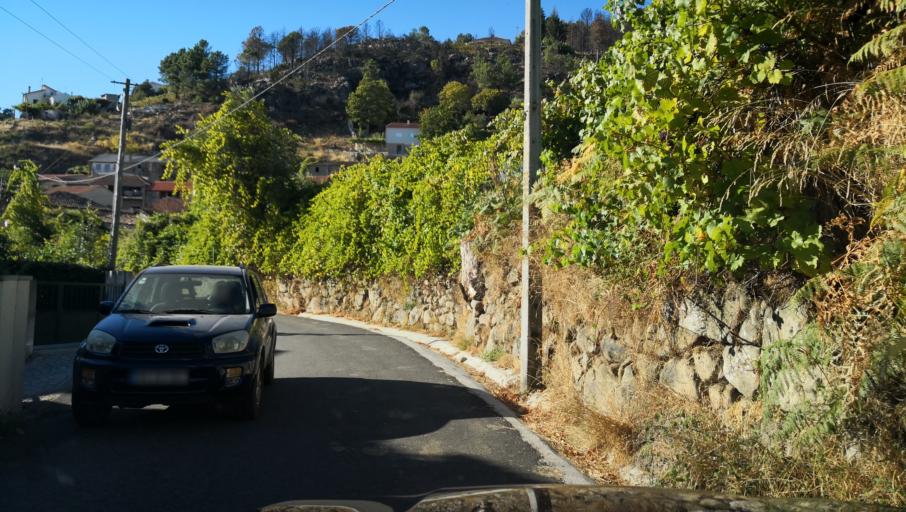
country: PT
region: Vila Real
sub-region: Vila Real
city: Vila Real
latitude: 41.3325
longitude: -7.7677
